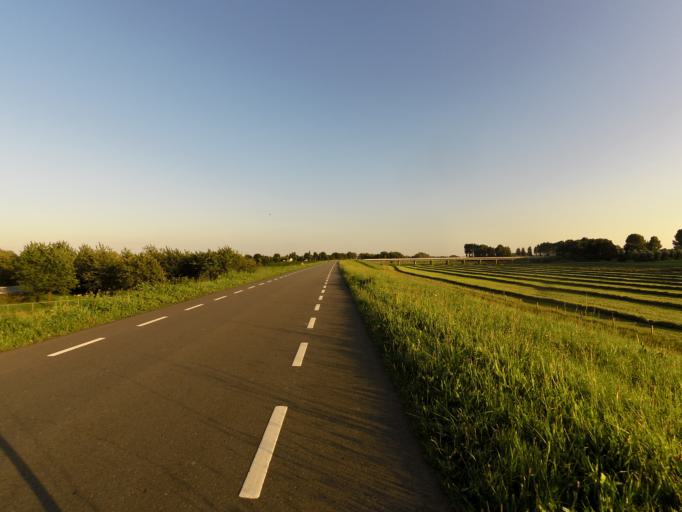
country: NL
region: Gelderland
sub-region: Gemeente Duiven
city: Duiven
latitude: 51.8946
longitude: 6.0291
